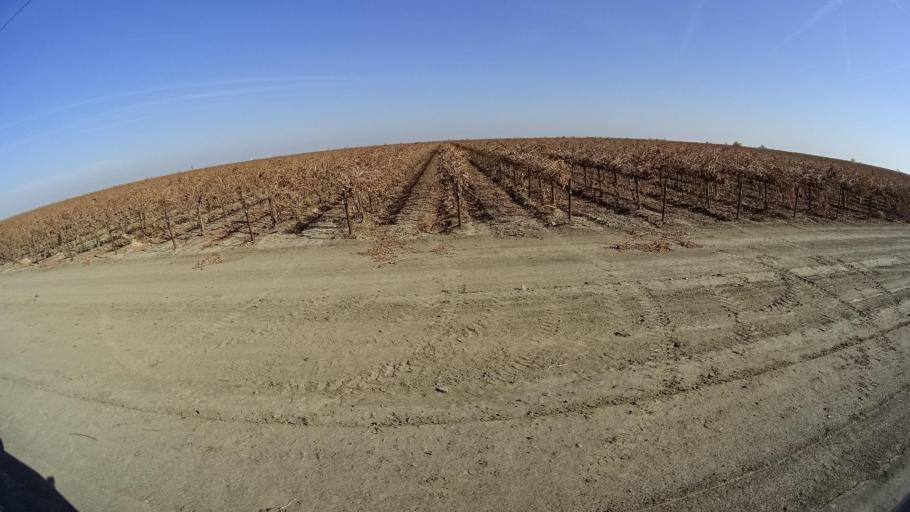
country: US
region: California
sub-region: Kern County
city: Wasco
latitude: 35.6863
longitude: -119.3839
